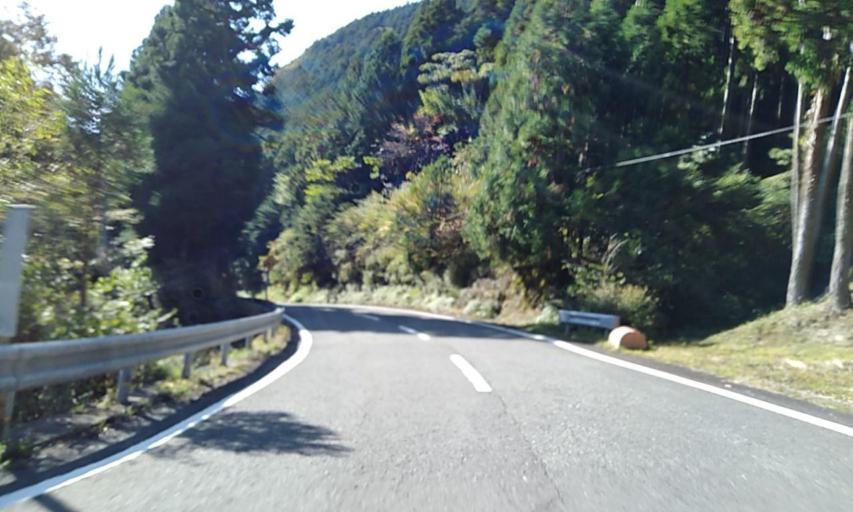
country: JP
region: Wakayama
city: Iwade
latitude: 34.1104
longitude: 135.3449
